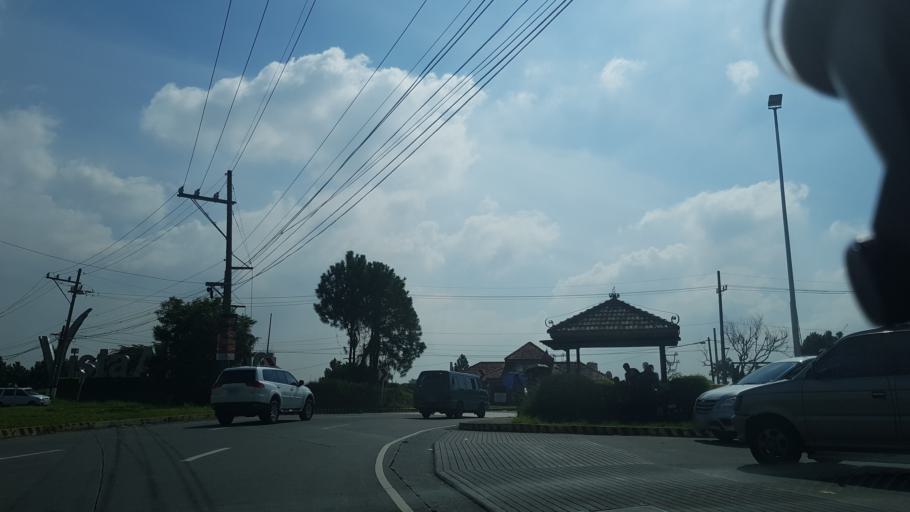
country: PH
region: Calabarzon
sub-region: Province of Laguna
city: San Pedro
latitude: 14.3748
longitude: 121.0119
